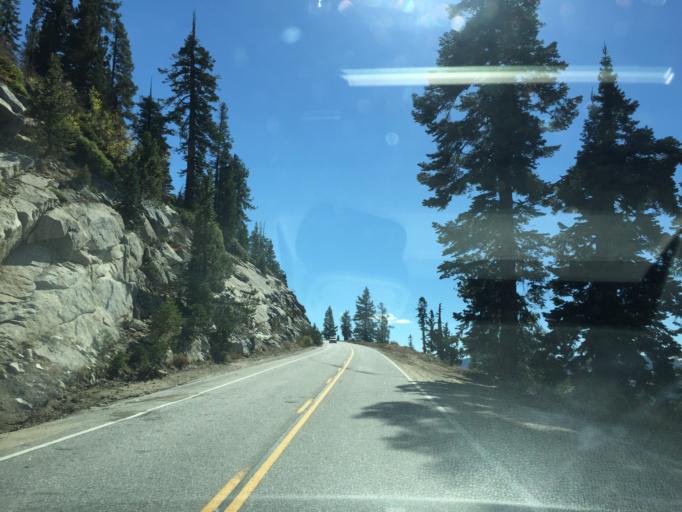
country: US
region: California
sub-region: Mariposa County
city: Yosemite Valley
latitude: 37.8304
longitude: -119.5798
